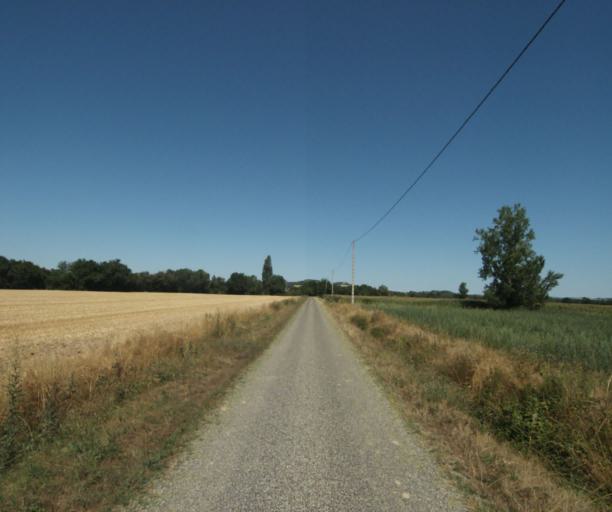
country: FR
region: Midi-Pyrenees
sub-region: Departement de la Haute-Garonne
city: Revel
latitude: 43.4796
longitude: 1.9564
